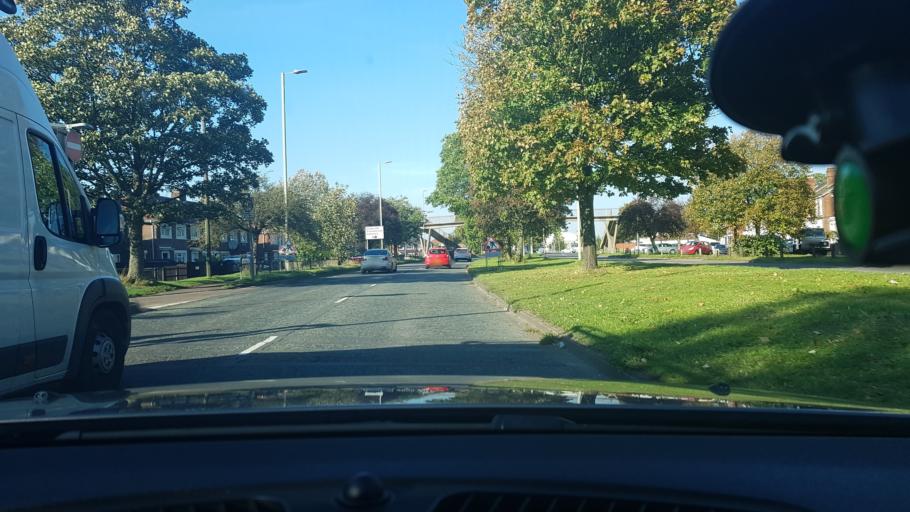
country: GB
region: England
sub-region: Gloucestershire
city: Gloucester
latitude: 51.8524
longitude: -2.2250
